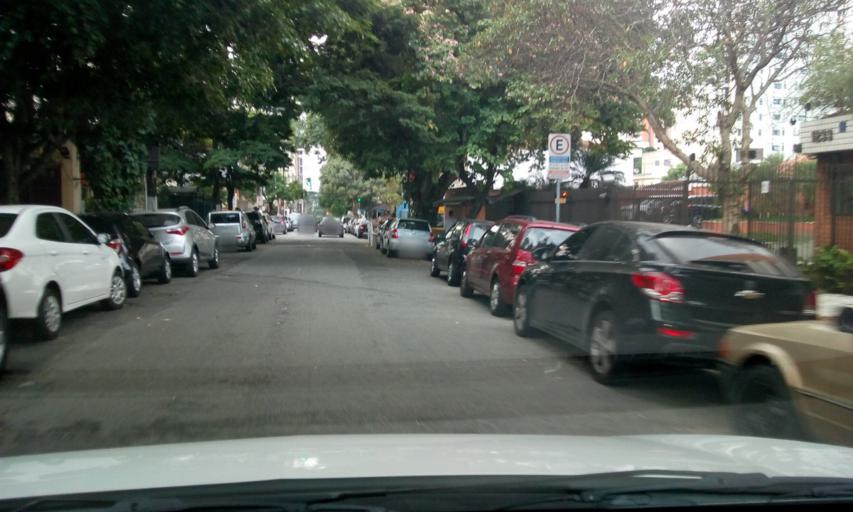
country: BR
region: Sao Paulo
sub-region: Sao Paulo
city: Sao Paulo
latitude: -23.6049
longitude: -46.6718
